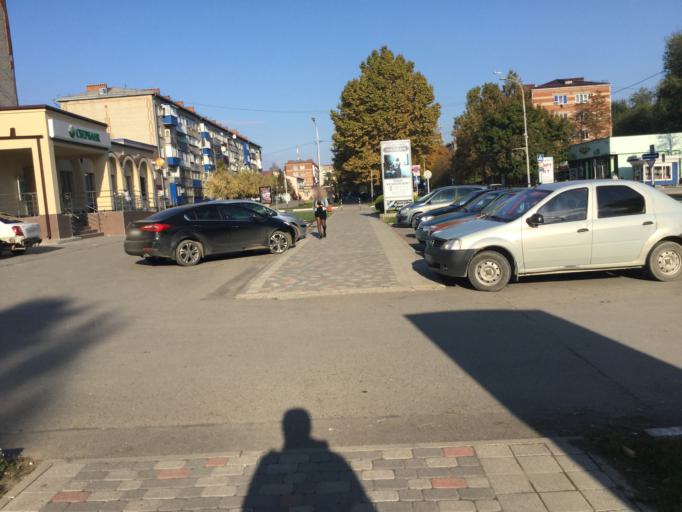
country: RU
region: Krasnodarskiy
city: Slavyansk-na-Kubani
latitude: 45.2554
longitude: 38.1155
